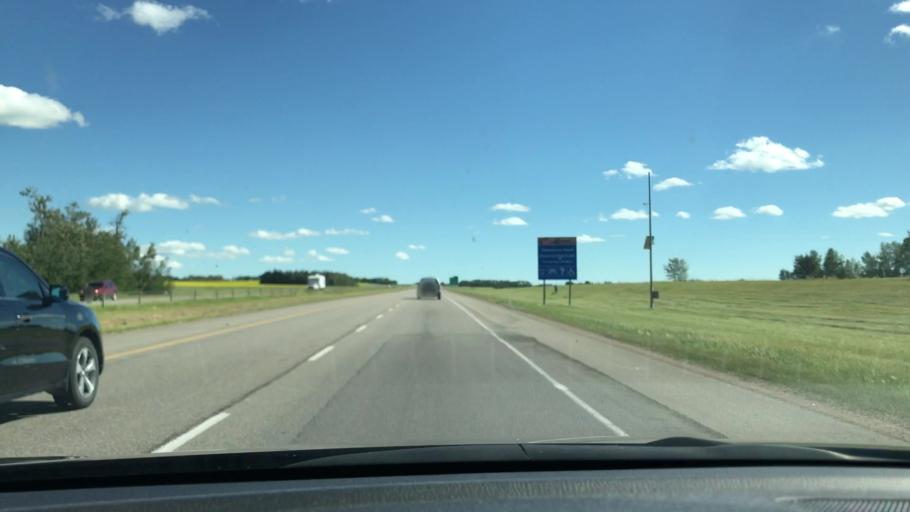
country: CA
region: Alberta
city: Penhold
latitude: 52.1668
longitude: -113.8141
